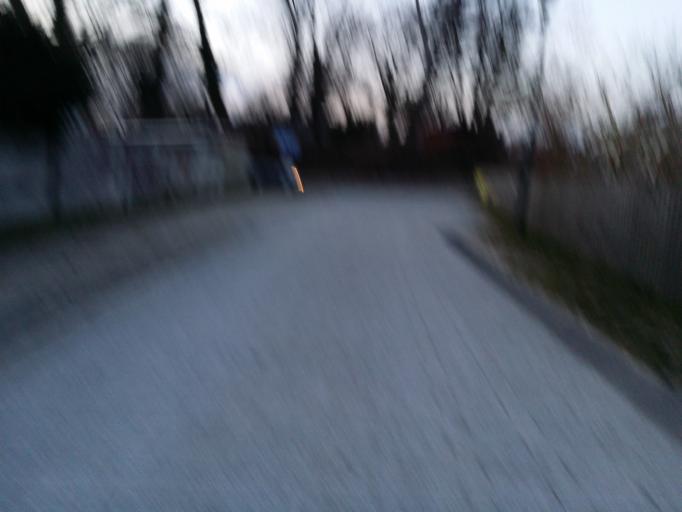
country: DE
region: Mecklenburg-Vorpommern
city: Koserow
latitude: 54.0498
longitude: 14.0004
